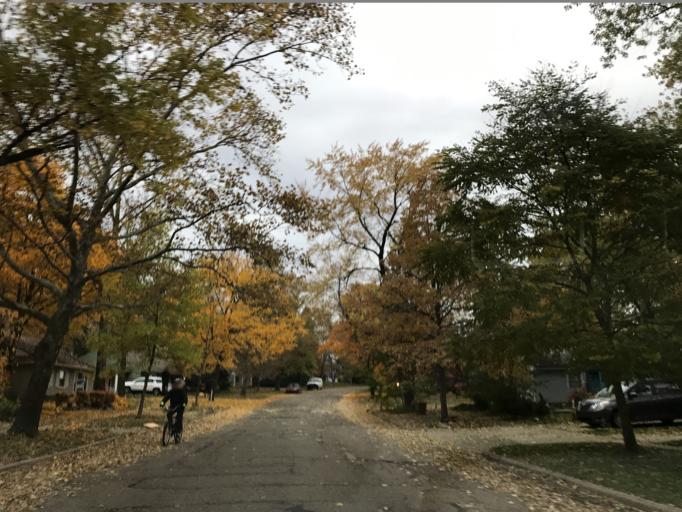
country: US
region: Michigan
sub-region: Washtenaw County
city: Ann Arbor
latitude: 42.2522
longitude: -83.6889
